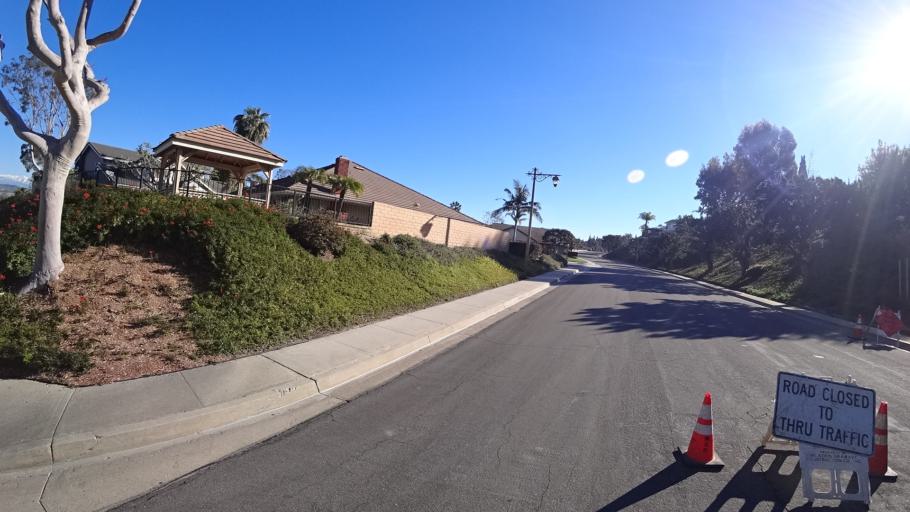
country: US
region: California
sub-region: Orange County
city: Villa Park
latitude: 33.8390
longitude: -117.8183
